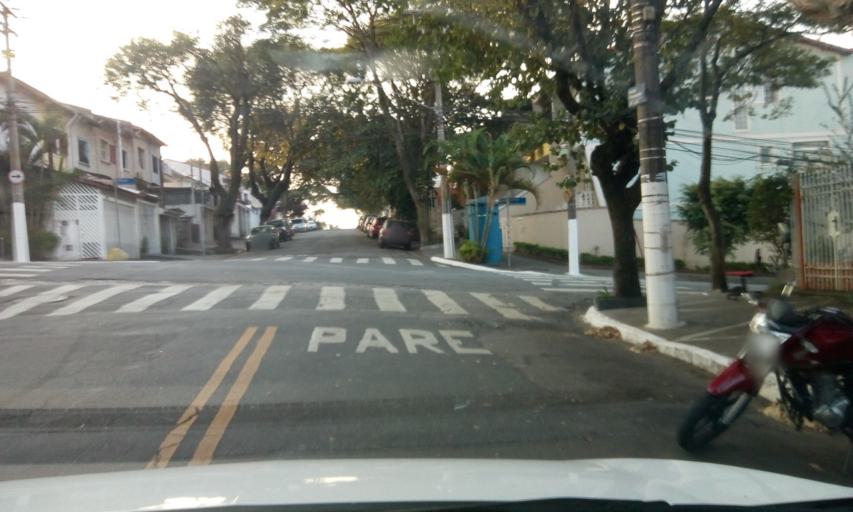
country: BR
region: Sao Paulo
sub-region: Sao Paulo
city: Sao Paulo
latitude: -23.6180
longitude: -46.6459
